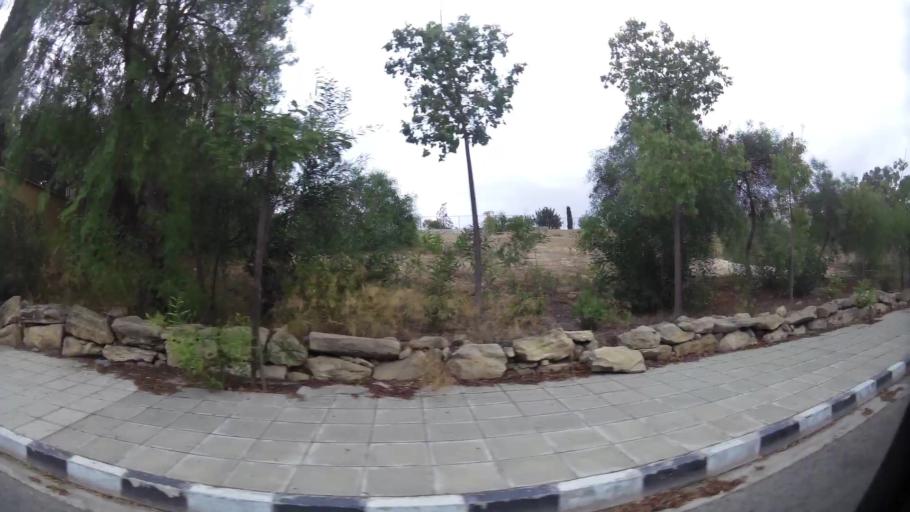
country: CY
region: Lefkosia
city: Geri
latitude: 35.1204
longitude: 33.3867
